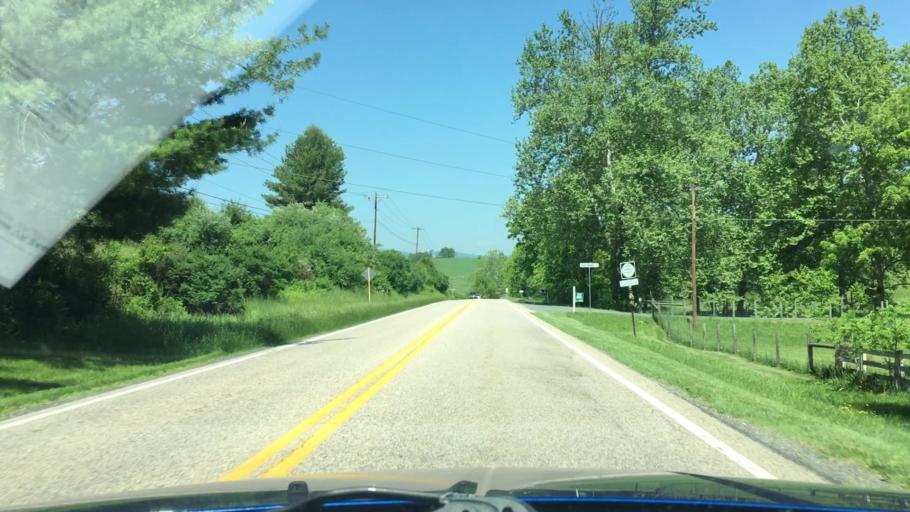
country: US
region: Virginia
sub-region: City of Staunton
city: Staunton
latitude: 38.1902
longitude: -79.1079
